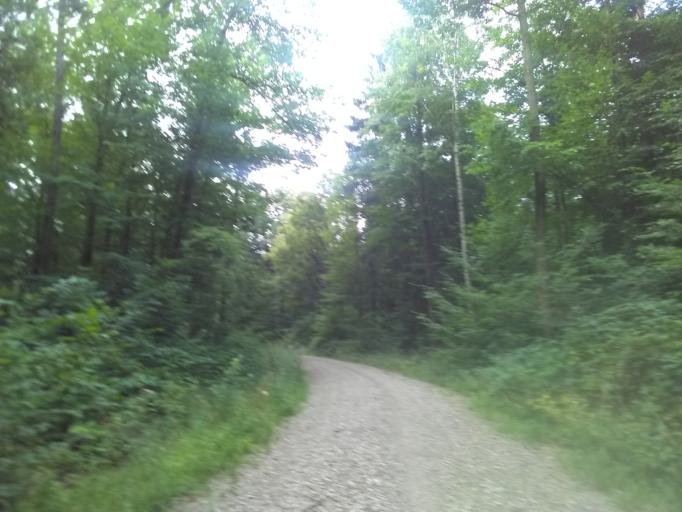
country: DE
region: Bavaria
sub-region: Upper Franconia
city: Pettstadt
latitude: 49.8503
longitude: 10.9108
